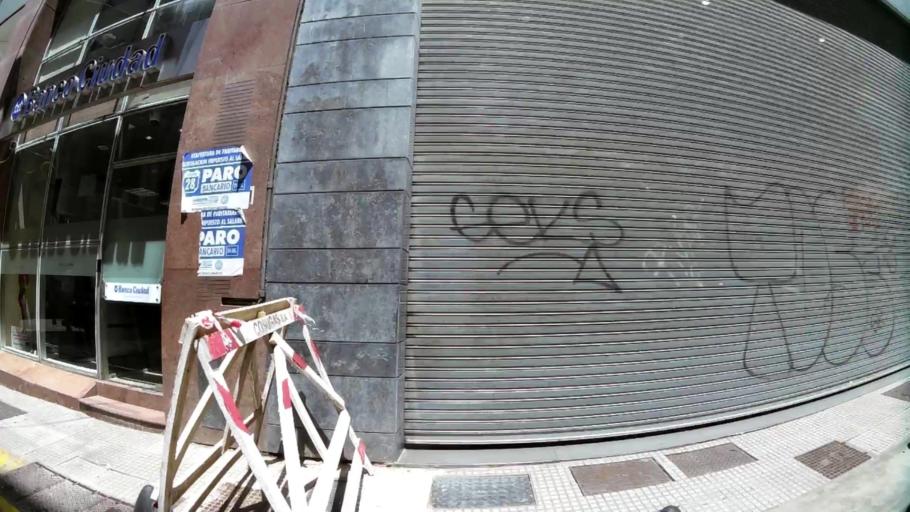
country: AR
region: Buenos Aires F.D.
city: Buenos Aires
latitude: -34.6042
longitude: -58.3707
